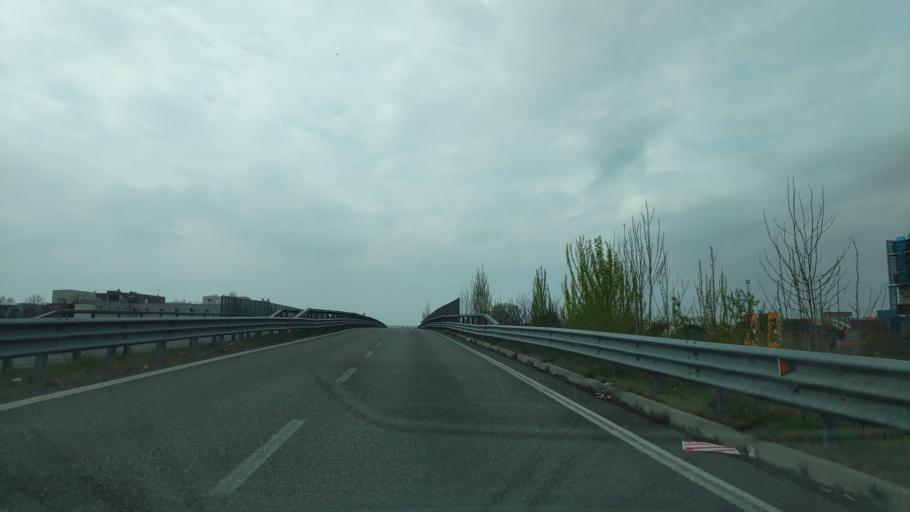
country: IT
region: Lombardy
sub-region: Citta metropolitana di Milano
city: San Bovio-San Felice
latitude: 45.4780
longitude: 9.3060
